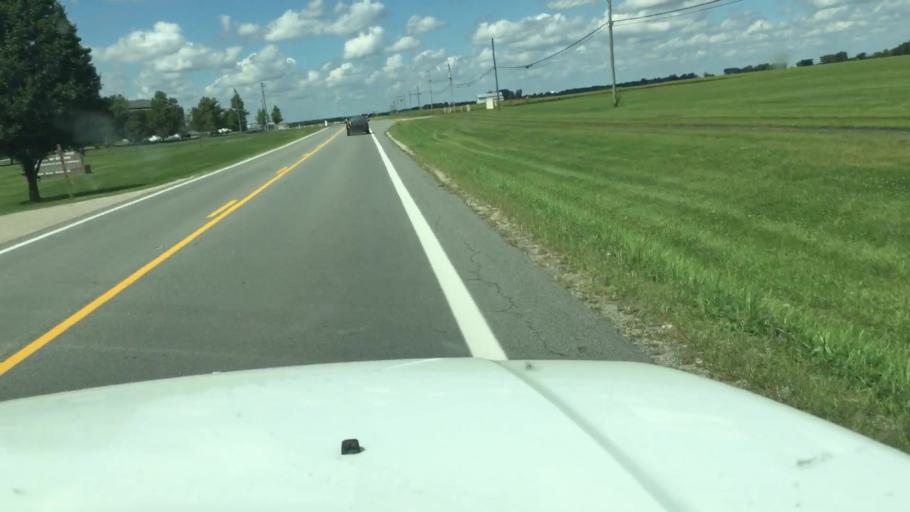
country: US
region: Ohio
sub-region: Madison County
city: London
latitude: 39.9106
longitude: -83.4747
